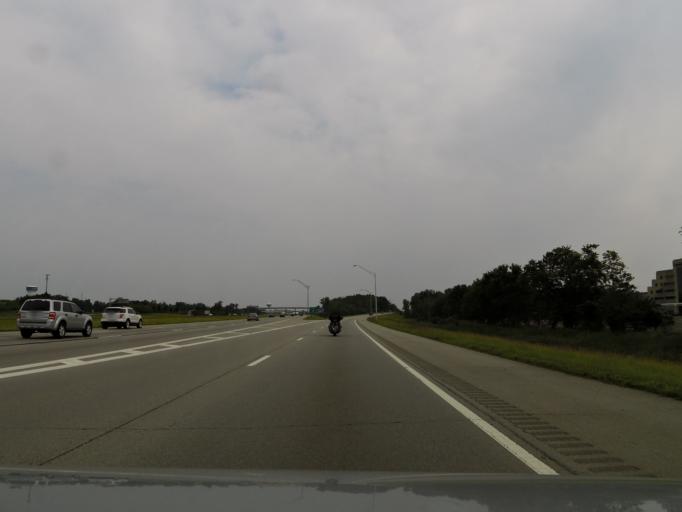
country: US
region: Ohio
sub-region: Warren County
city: Five Points
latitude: 39.6129
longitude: -84.2325
